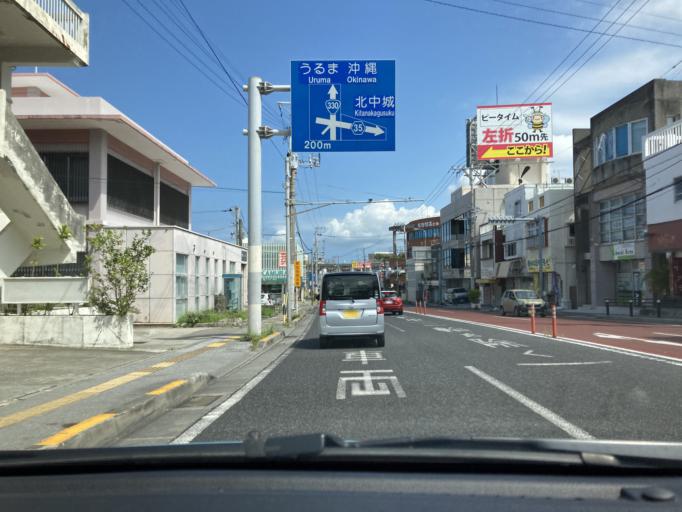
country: JP
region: Okinawa
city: Chatan
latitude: 26.2881
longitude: 127.7776
